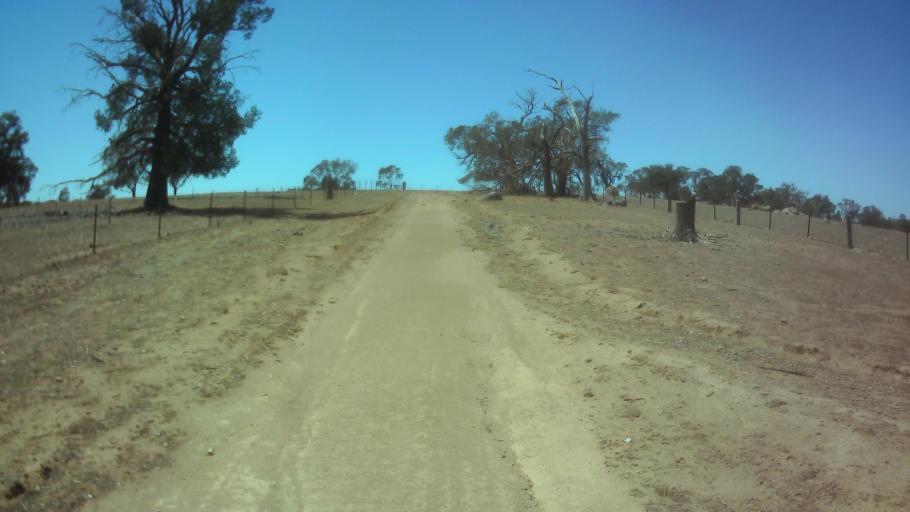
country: AU
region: New South Wales
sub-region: Cowra
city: Cowra
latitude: -33.8996
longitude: 148.5079
